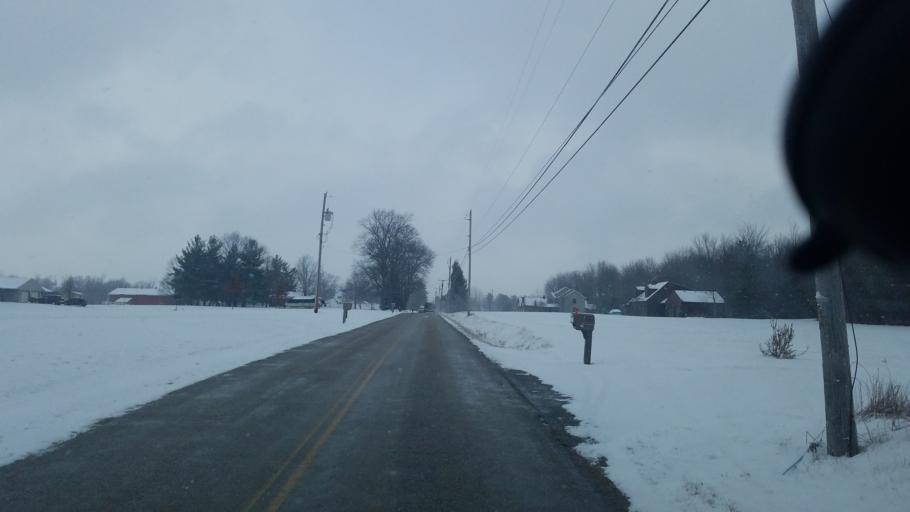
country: US
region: Ohio
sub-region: Richland County
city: Ontario
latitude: 40.7484
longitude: -82.6469
